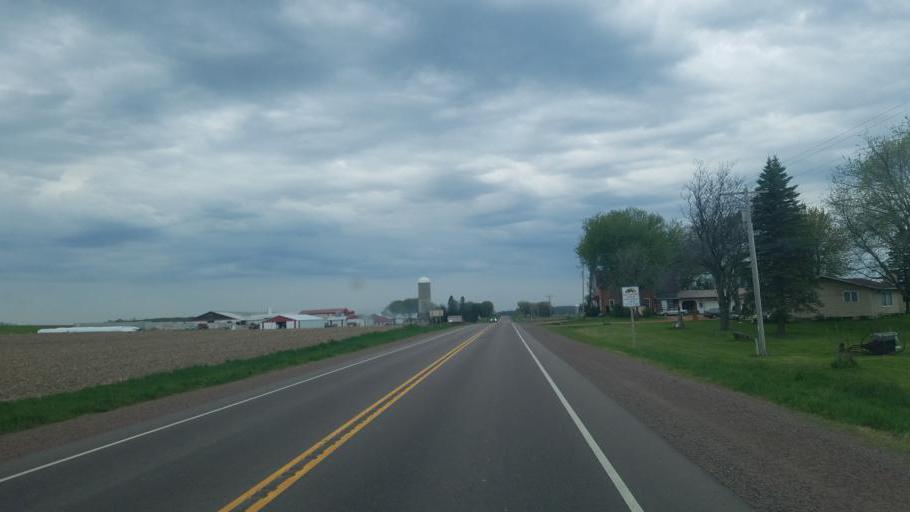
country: US
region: Wisconsin
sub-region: Wood County
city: Marshfield
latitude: 44.5989
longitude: -90.2996
